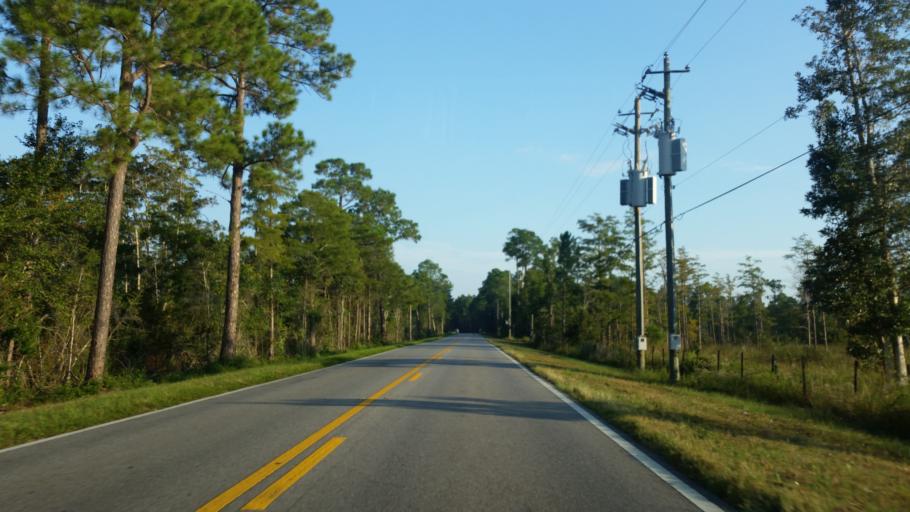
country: US
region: Florida
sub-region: Santa Rosa County
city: East Milton
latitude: 30.5999
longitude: -87.0070
